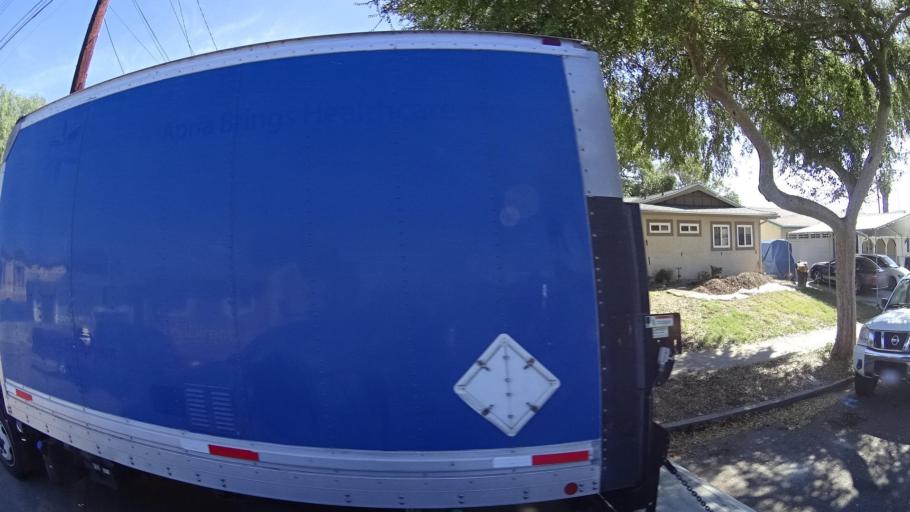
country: US
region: California
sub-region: San Diego County
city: Lemon Grove
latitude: 32.7236
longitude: -117.0193
